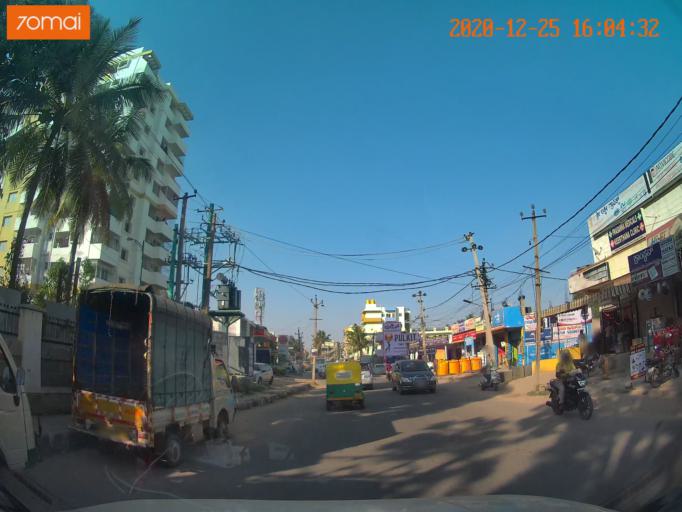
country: IN
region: Karnataka
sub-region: Bangalore Urban
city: Bangalore
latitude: 12.8864
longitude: 77.6255
